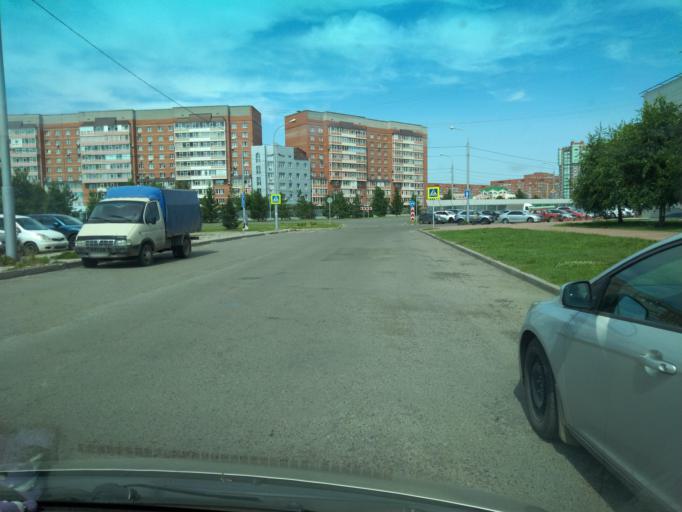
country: RU
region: Krasnoyarskiy
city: Krasnoyarsk
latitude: 56.0506
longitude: 92.9129
